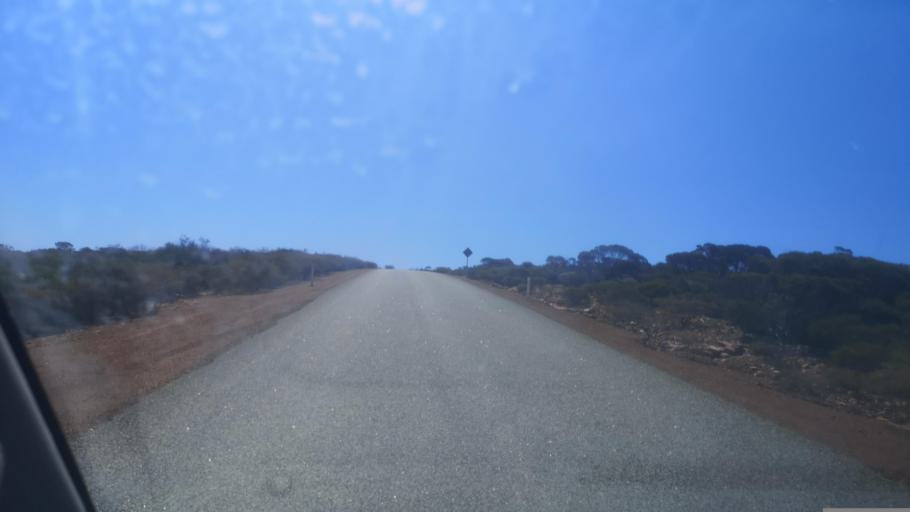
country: AU
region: Western Australia
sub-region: Northampton Shire
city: Kalbarri
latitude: -27.8171
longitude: 114.4697
